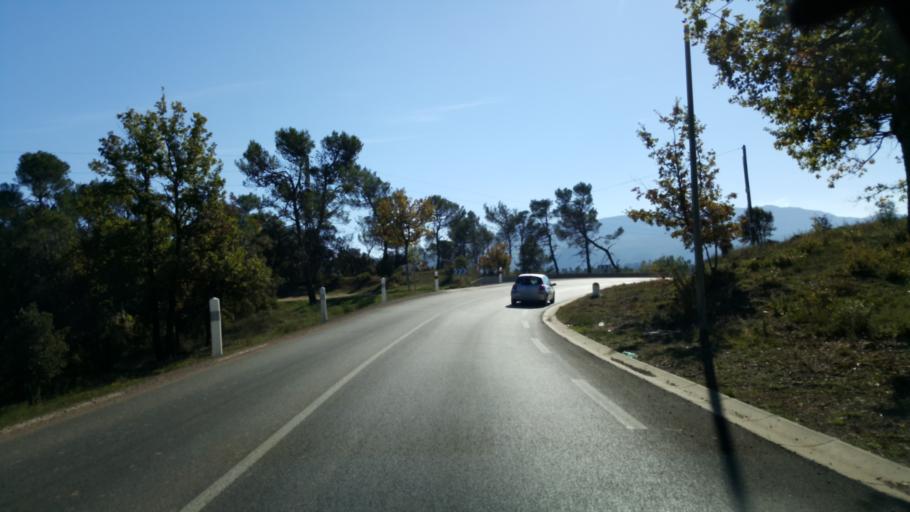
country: FR
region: Provence-Alpes-Cote d'Azur
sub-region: Departement du Var
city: Rougiers
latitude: 43.4096
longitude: 5.8254
